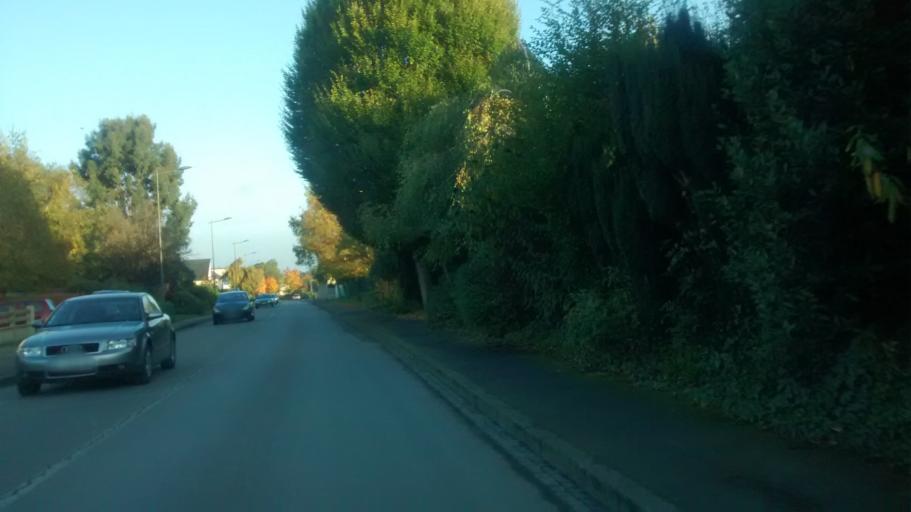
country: FR
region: Brittany
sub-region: Departement d'Ille-et-Vilaine
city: Le Rheu
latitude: 48.1253
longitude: -1.8143
